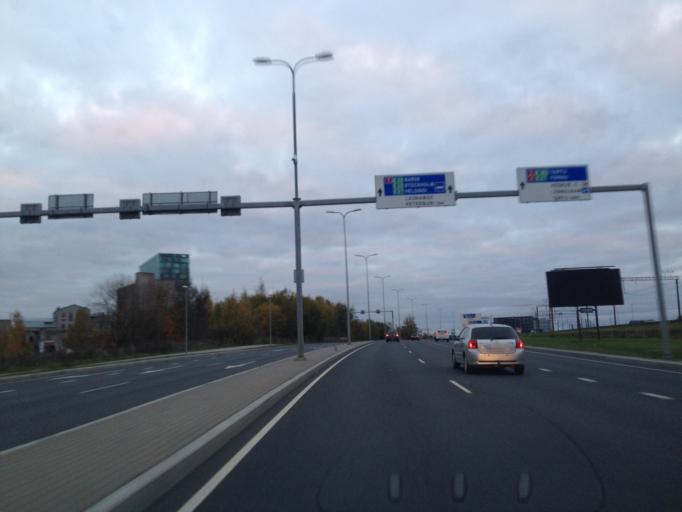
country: EE
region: Harju
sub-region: Tallinna linn
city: Tallinn
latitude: 59.4230
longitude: 24.7759
